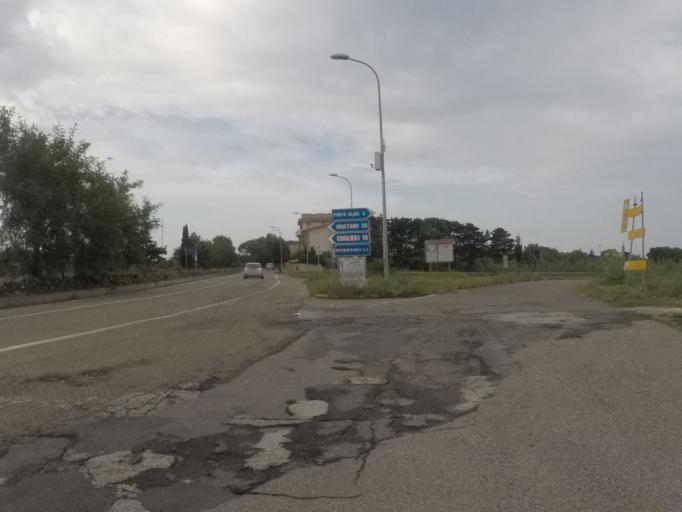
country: IT
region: Sardinia
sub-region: Provincia di Oristano
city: Magomadas
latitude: 40.2595
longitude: 8.5254
